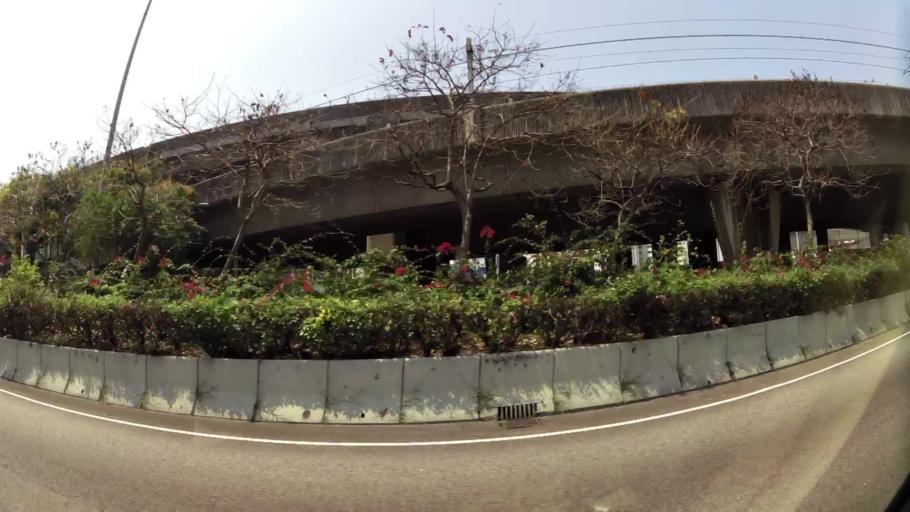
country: HK
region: Sham Shui Po
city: Sham Shui Po
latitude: 22.3428
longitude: 114.1300
